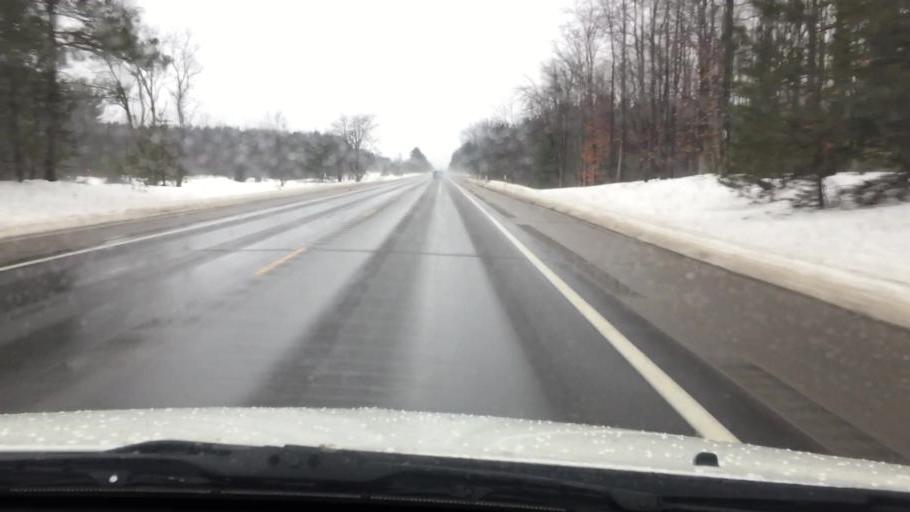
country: US
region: Michigan
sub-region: Kalkaska County
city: Kalkaska
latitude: 44.6919
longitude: -85.2142
